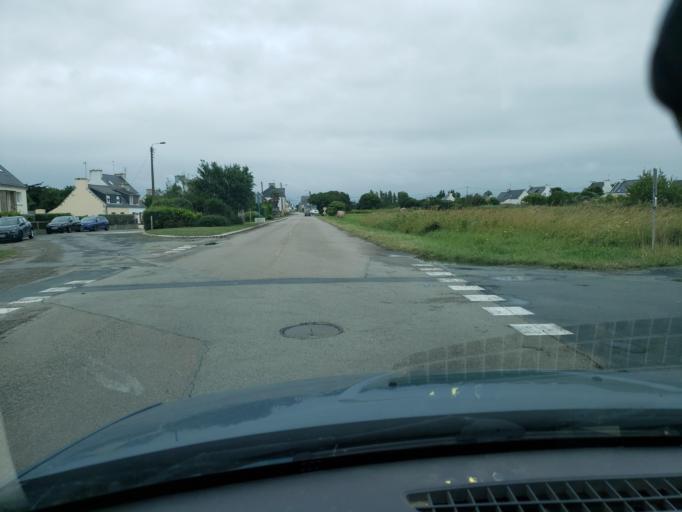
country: FR
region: Brittany
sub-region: Departement du Finistere
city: Guilvinec
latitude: 47.8056
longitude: -4.3508
